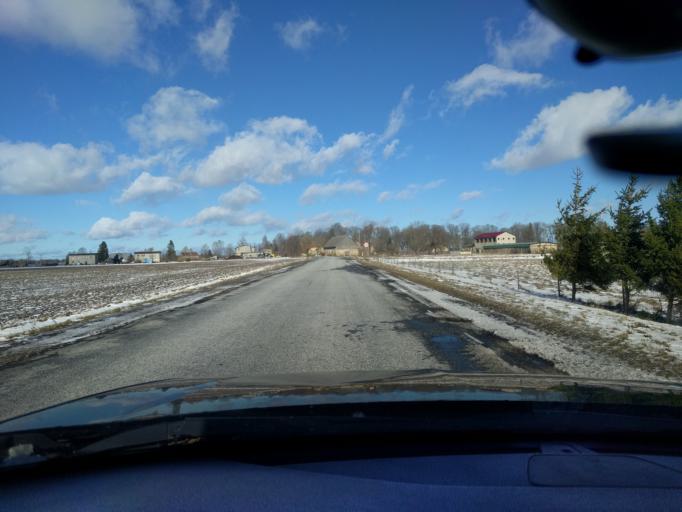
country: EE
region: Harju
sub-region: Raasiku vald
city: Raasiku
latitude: 59.3327
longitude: 25.1566
